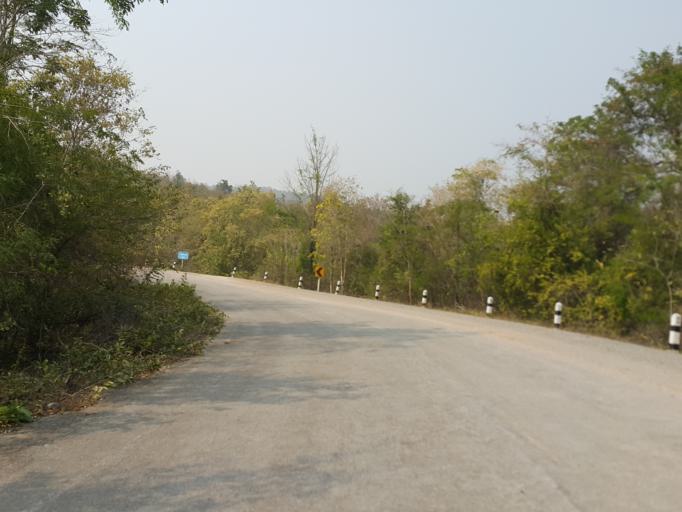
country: TH
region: Lampang
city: Mae Phrik
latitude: 17.5034
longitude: 99.0830
